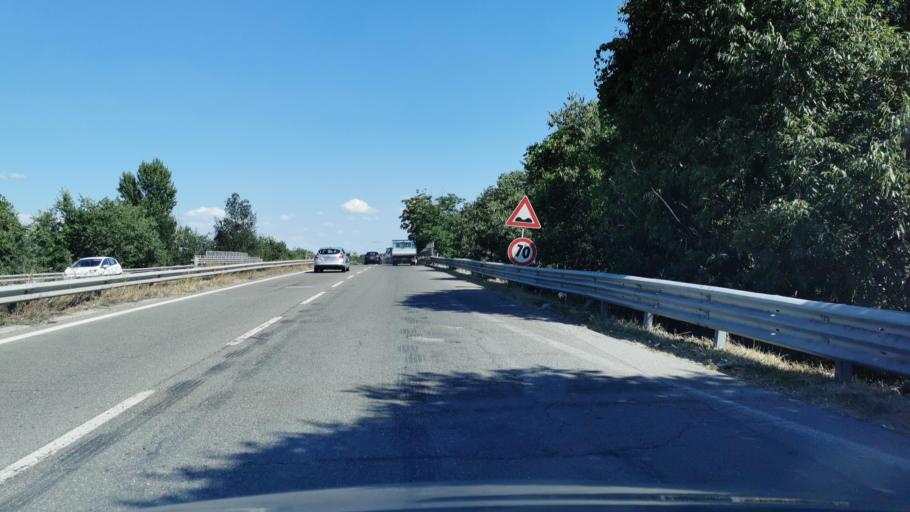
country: IT
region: Emilia-Romagna
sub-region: Provincia di Modena
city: Modena
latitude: 44.6644
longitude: 10.9377
